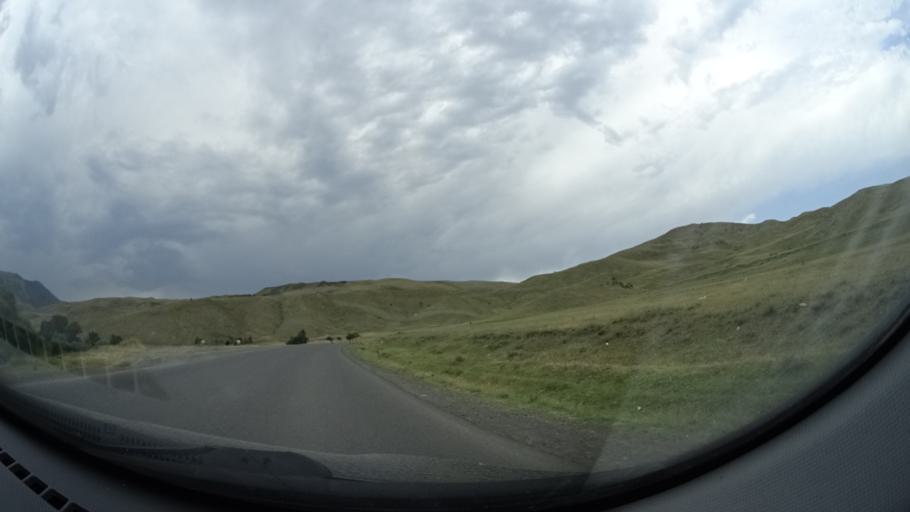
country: GE
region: Samtskhe-Javakheti
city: Aspindza
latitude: 41.5969
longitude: 43.1958
